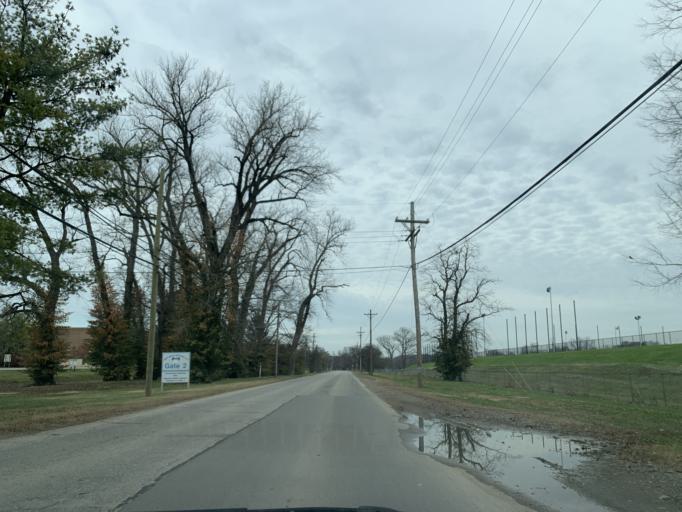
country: US
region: Indiana
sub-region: Clark County
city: Jeffersonville
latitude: 38.2700
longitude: -85.7120
